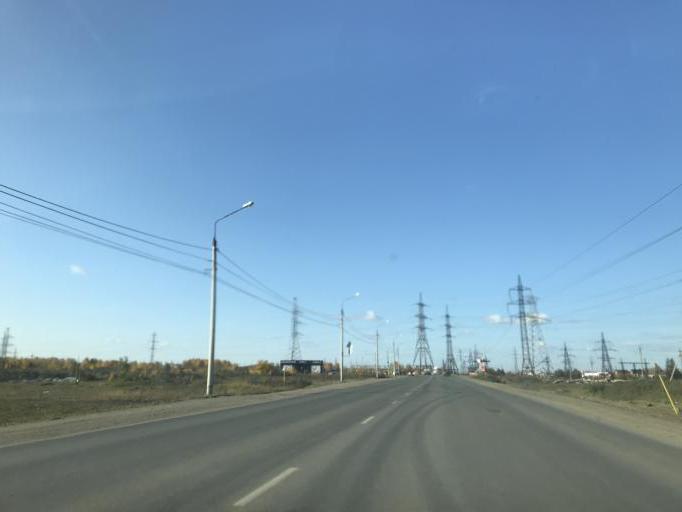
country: RU
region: Chelyabinsk
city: Roshchino
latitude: 55.2234
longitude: 61.2930
